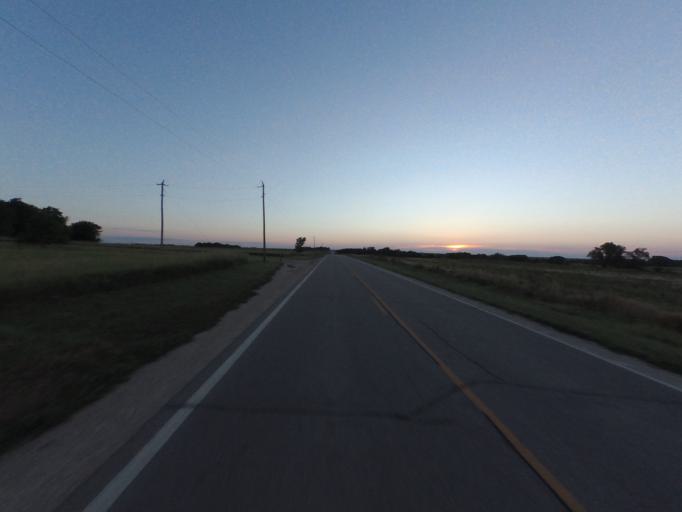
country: US
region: Kansas
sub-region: Rice County
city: Sterling
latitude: 38.1446
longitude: -98.1854
